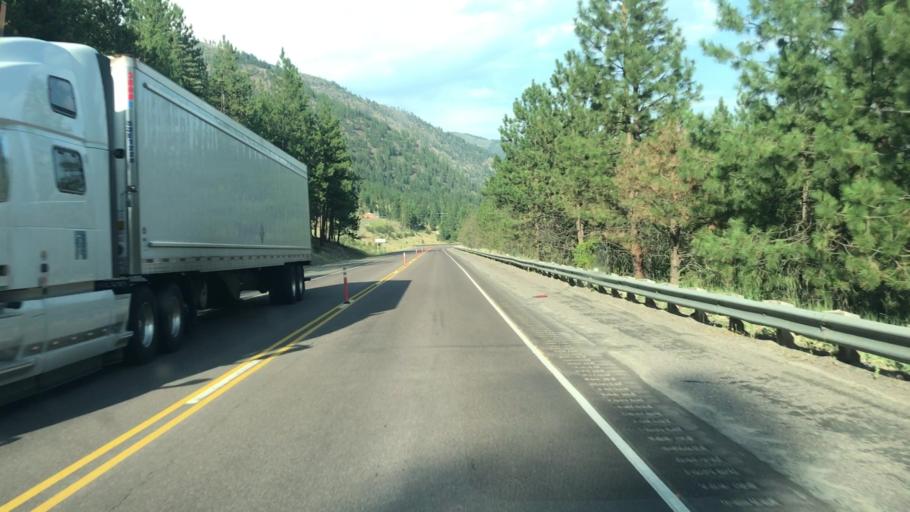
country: US
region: Montana
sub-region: Mineral County
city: Superior
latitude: 47.0176
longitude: -114.6837
